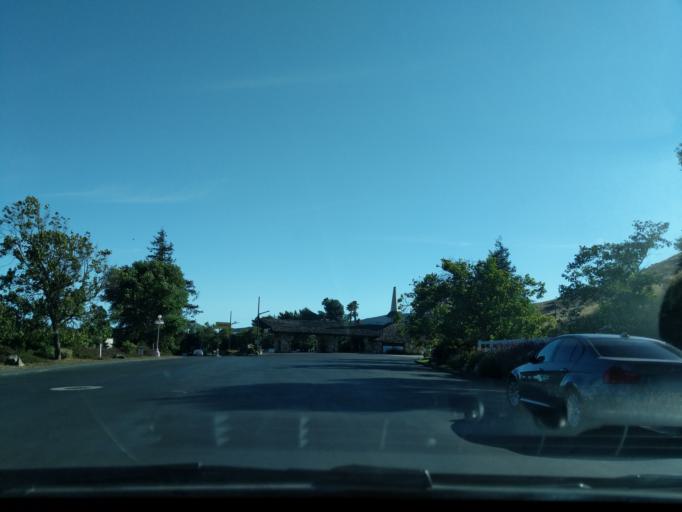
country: US
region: California
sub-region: San Luis Obispo County
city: San Luis Obispo
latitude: 35.2664
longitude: -120.6753
